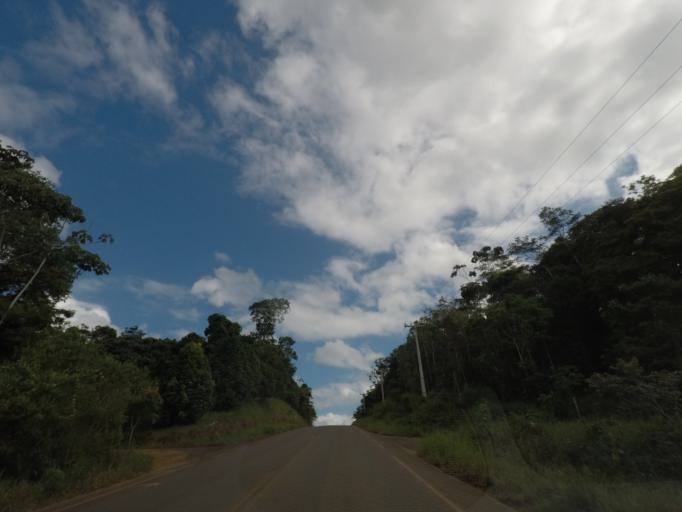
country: BR
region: Bahia
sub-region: Itacare
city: Itacare
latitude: -14.2180
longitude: -39.0996
